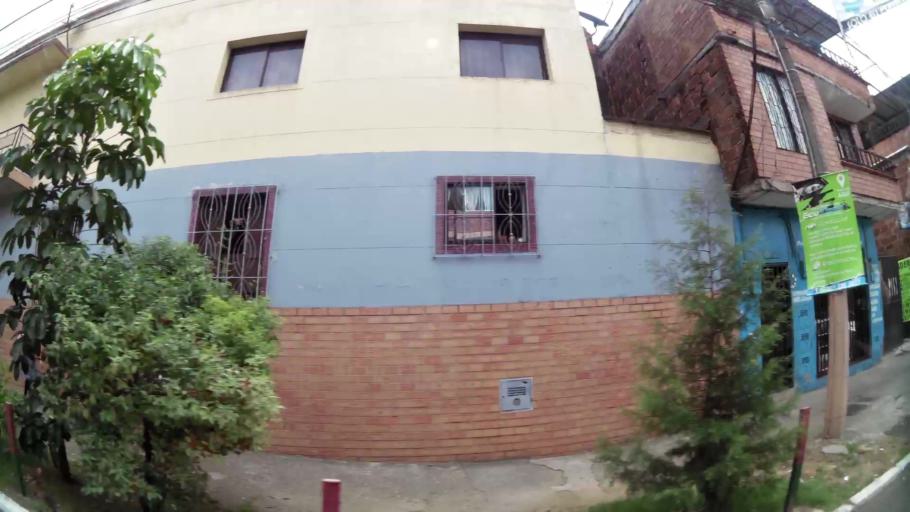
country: CO
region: Antioquia
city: Medellin
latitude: 6.2719
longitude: -75.5553
